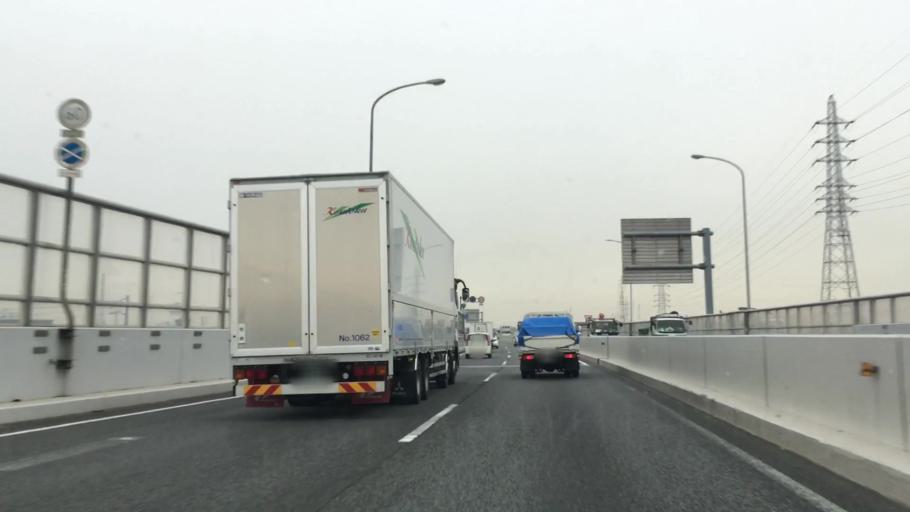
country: JP
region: Aichi
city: Chiryu
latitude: 34.9996
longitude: 137.0293
